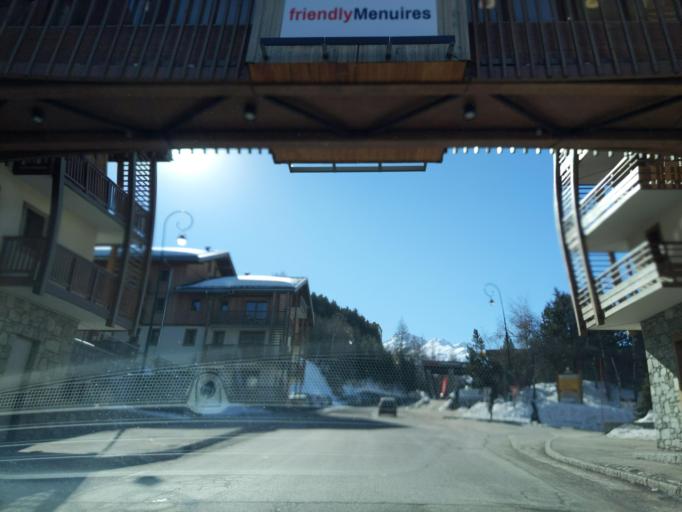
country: FR
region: Rhone-Alpes
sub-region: Departement de la Savoie
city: Saint-Martin-de-Belleville
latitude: 45.3324
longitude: 6.5361
